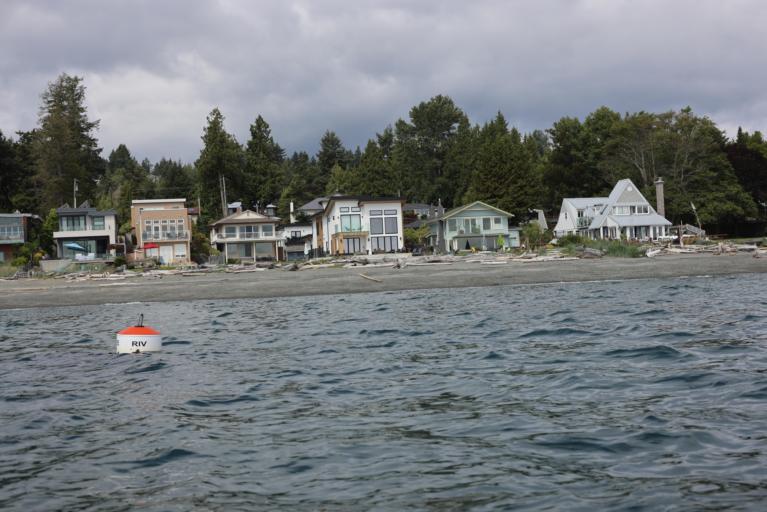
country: CA
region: British Columbia
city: Victoria
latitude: 48.5240
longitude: -123.3642
